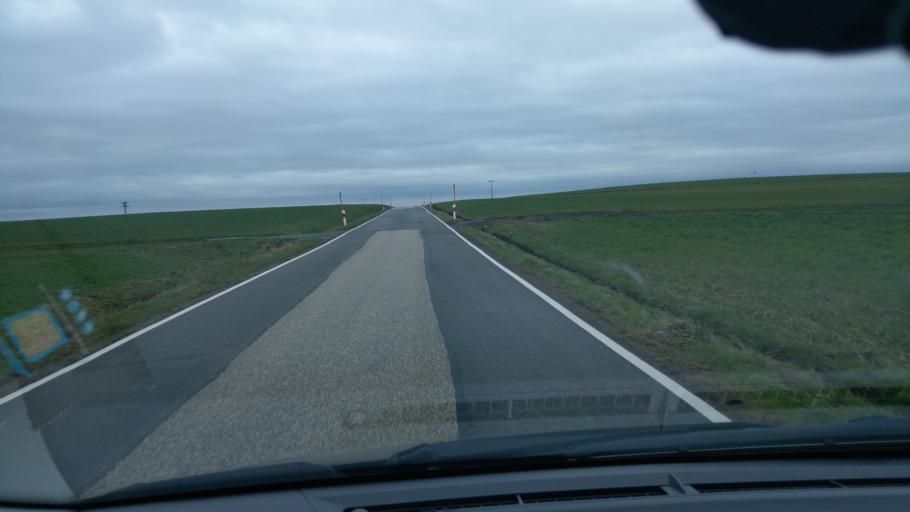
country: DE
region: Rheinland-Pfalz
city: Kleinbundenbach
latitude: 49.3257
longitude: 7.4325
